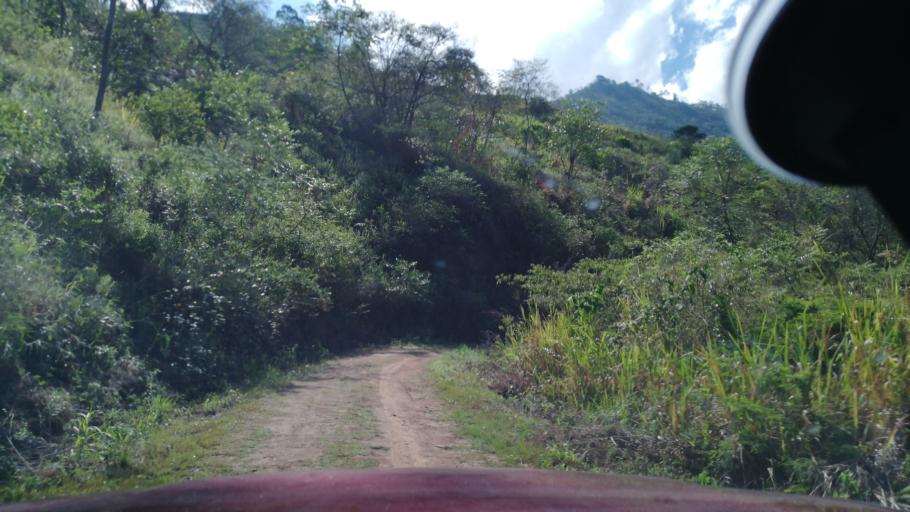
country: CO
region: Cundinamarca
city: Quipile
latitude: 4.7409
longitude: -74.6100
